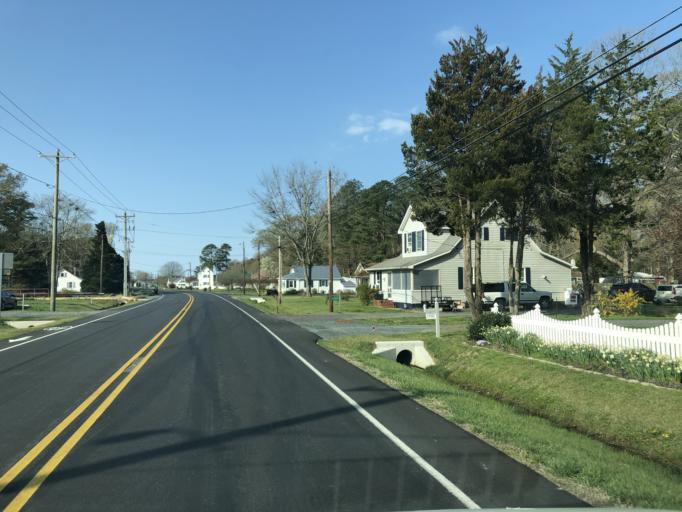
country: US
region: Maryland
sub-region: Dorchester County
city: Algonquin
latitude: 38.5098
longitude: -76.1448
